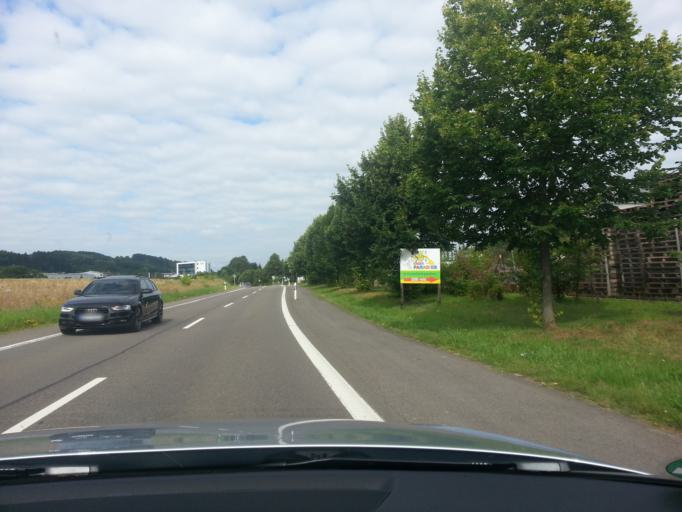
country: DE
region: Saarland
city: Losheim
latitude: 49.5025
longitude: 6.7656
